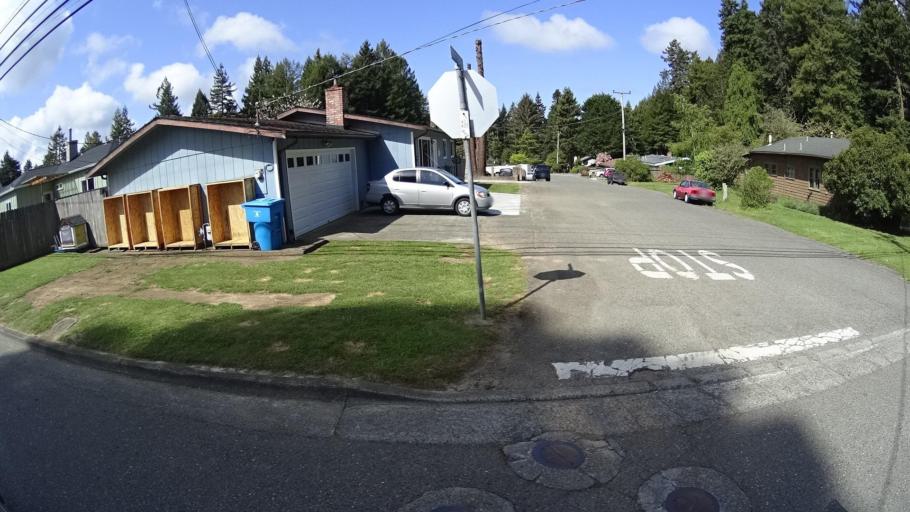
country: US
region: California
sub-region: Humboldt County
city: Cutten
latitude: 40.7620
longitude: -124.1542
